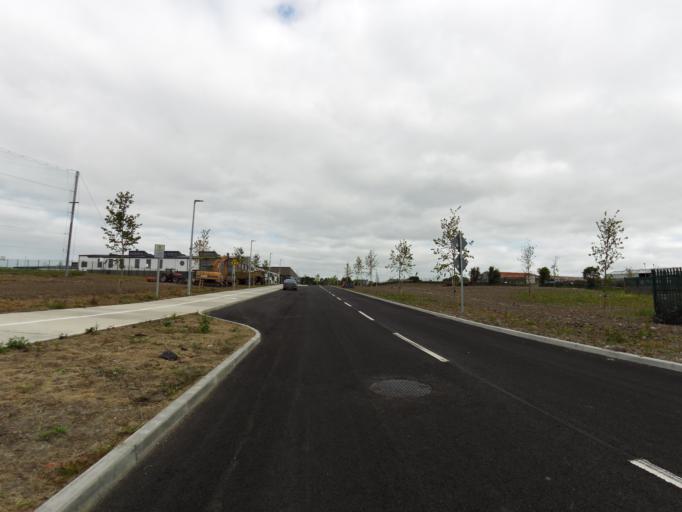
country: IE
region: Connaught
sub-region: County Galway
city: Athenry
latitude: 53.2919
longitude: -8.7527
